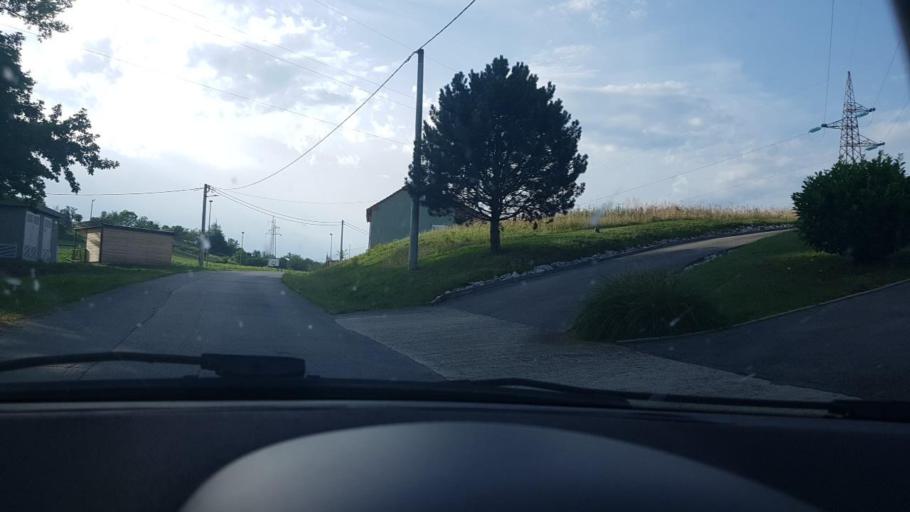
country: HR
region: Krapinsko-Zagorska
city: Zabok
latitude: 46.0326
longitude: 15.9161
